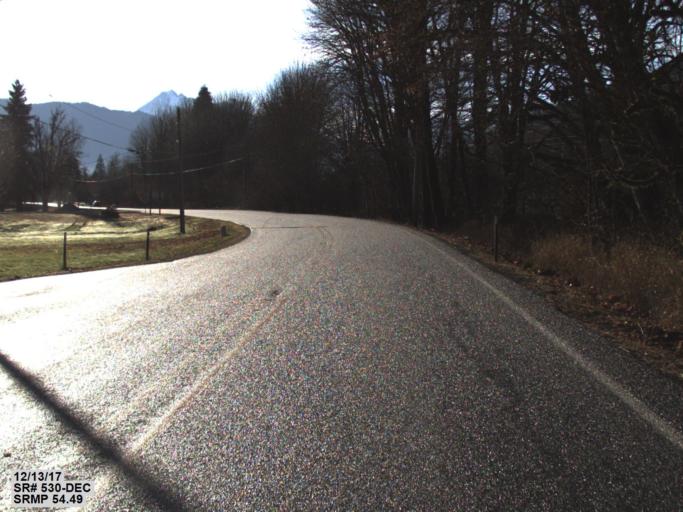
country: US
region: Washington
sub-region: Snohomish County
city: Darrington
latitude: 48.3213
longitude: -121.5545
